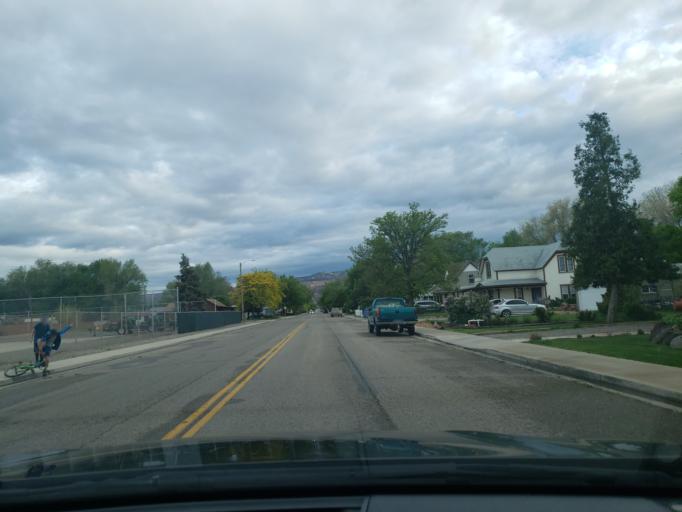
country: US
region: Colorado
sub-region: Mesa County
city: Fruita
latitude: 39.1633
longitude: -108.7314
